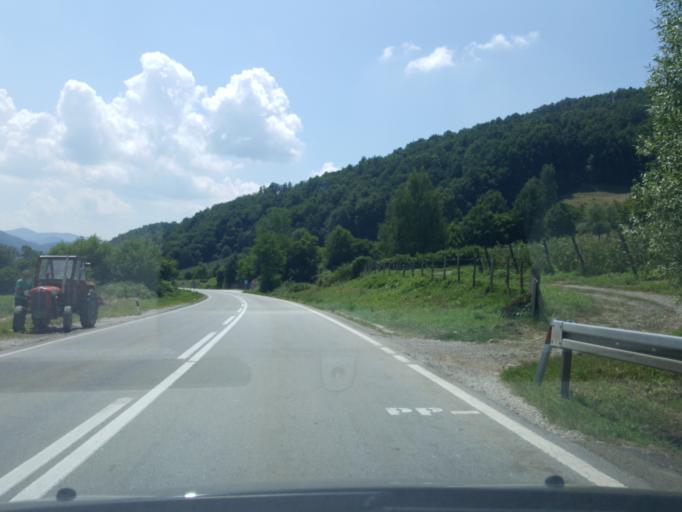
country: RS
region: Central Serbia
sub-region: Moravicki Okrug
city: Gornji Milanovac
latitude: 44.0857
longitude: 20.4798
